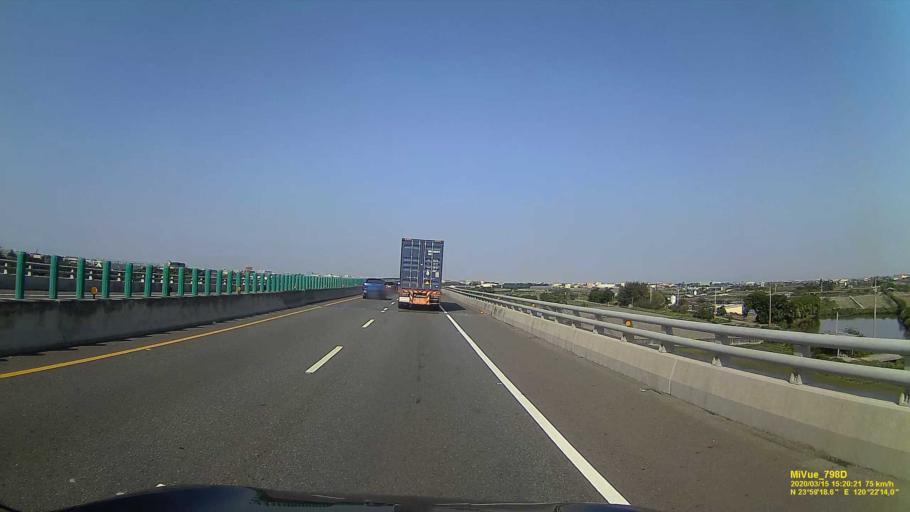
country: TW
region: Taiwan
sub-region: Changhua
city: Chang-hua
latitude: 23.9886
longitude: 120.3714
